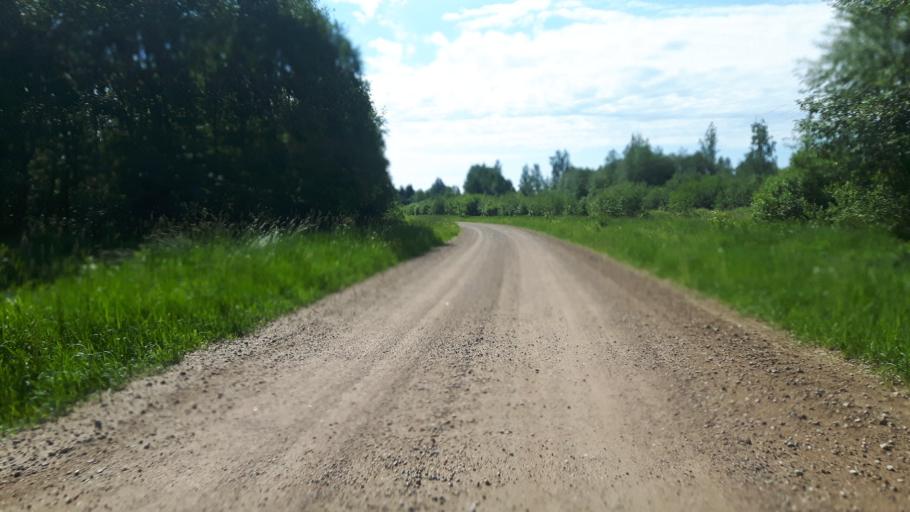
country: EE
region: Paernumaa
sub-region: Vaendra vald (alev)
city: Vandra
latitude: 58.6868
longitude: 25.0330
